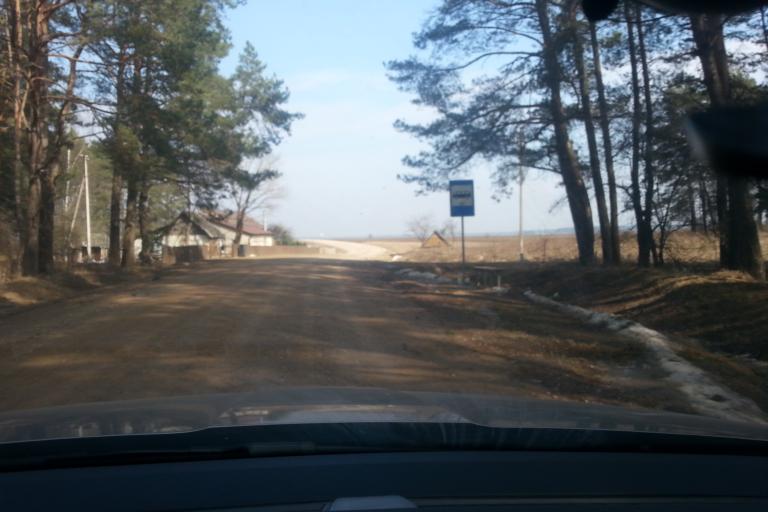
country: LT
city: Trakai
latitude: 54.5824
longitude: 24.9748
